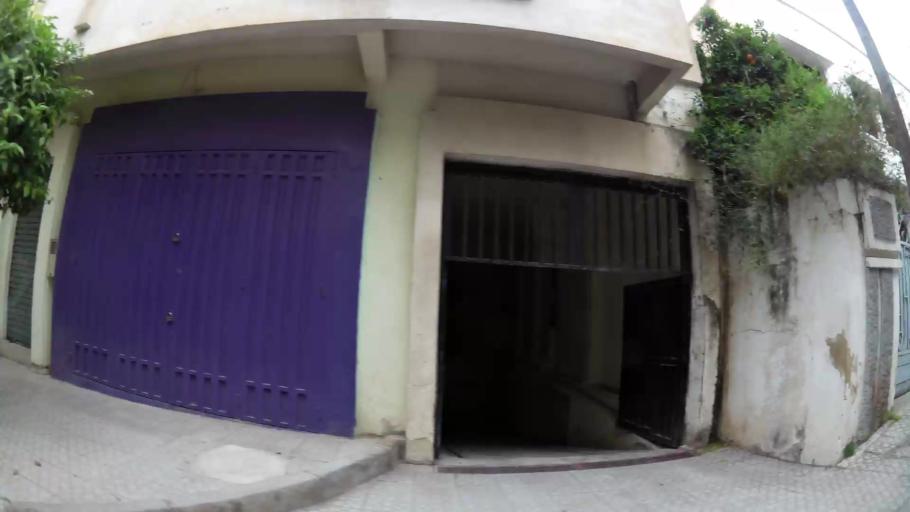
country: MA
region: Fes-Boulemane
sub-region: Fes
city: Fes
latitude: 34.0368
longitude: -4.9966
